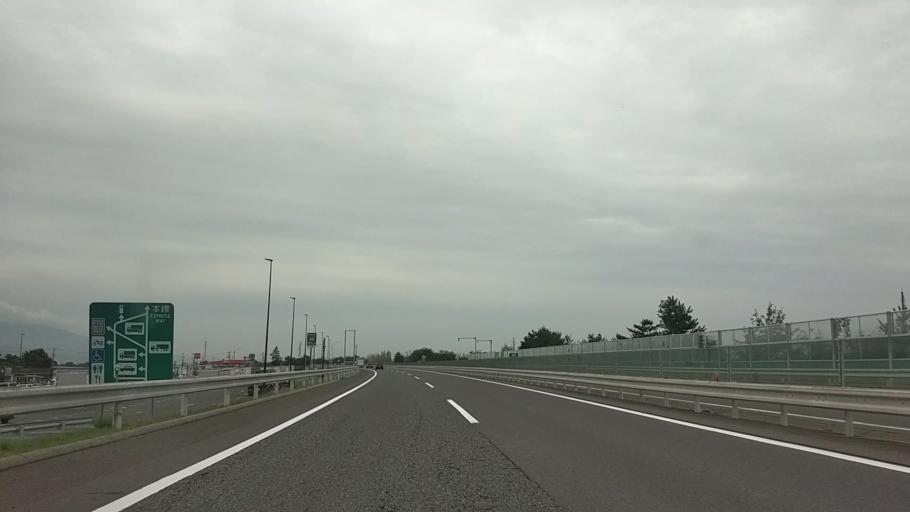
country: JP
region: Nagano
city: Toyoshina
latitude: 36.2723
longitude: 137.9309
